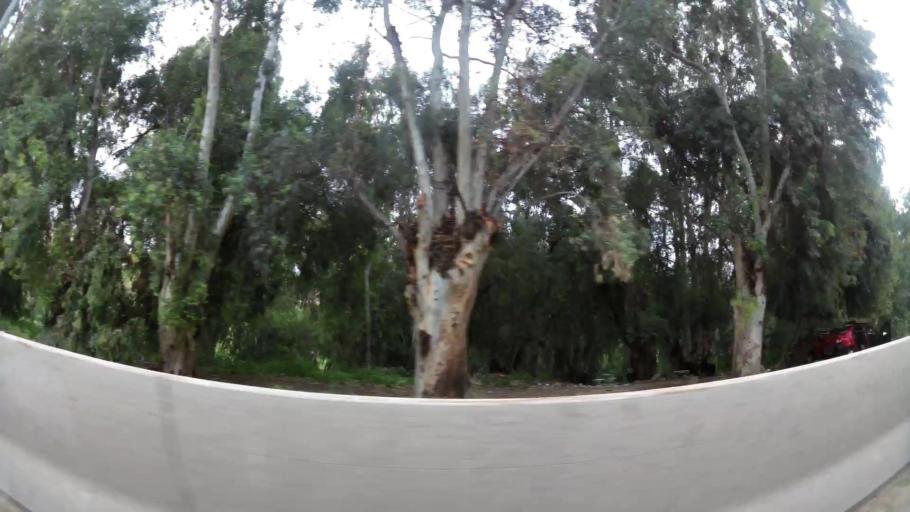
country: MA
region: Fes-Boulemane
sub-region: Fes
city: Fes
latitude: 34.0406
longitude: -4.9934
